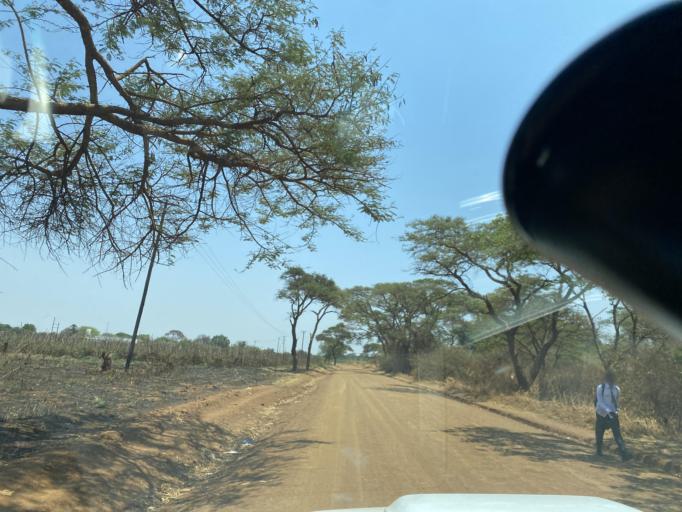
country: ZM
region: Lusaka
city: Lusaka
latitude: -15.4195
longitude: 28.1033
